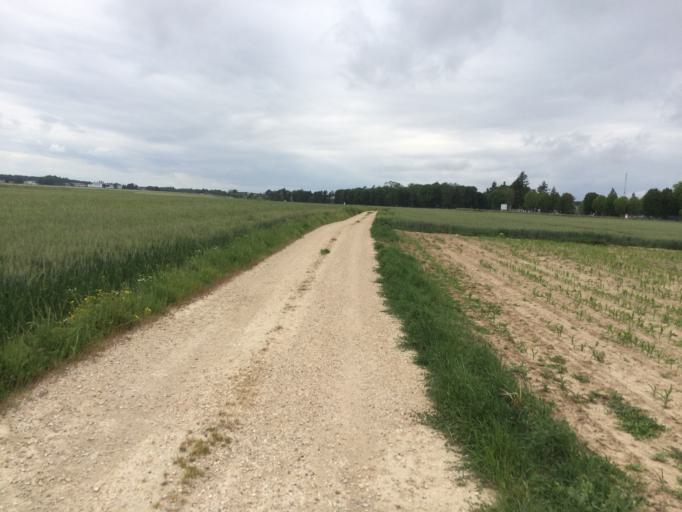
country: FR
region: Ile-de-France
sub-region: Departement de l'Essonne
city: Saclay
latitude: 48.7250
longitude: 2.1613
